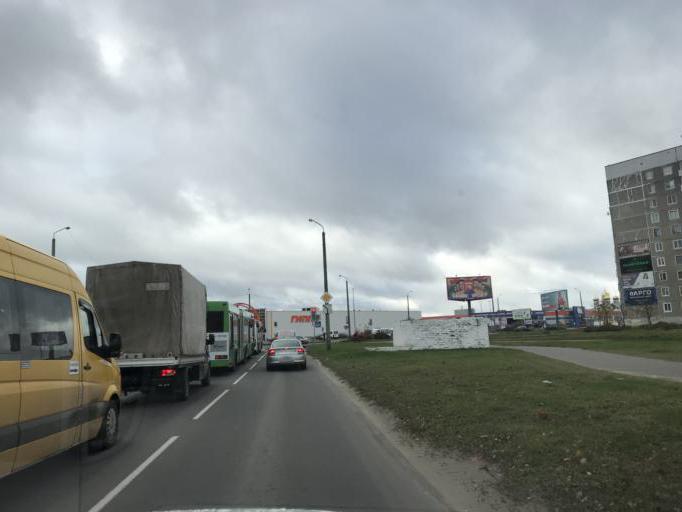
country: BY
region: Mogilev
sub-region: Mahilyowski Rayon
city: Veyno
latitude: 53.8739
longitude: 30.3648
